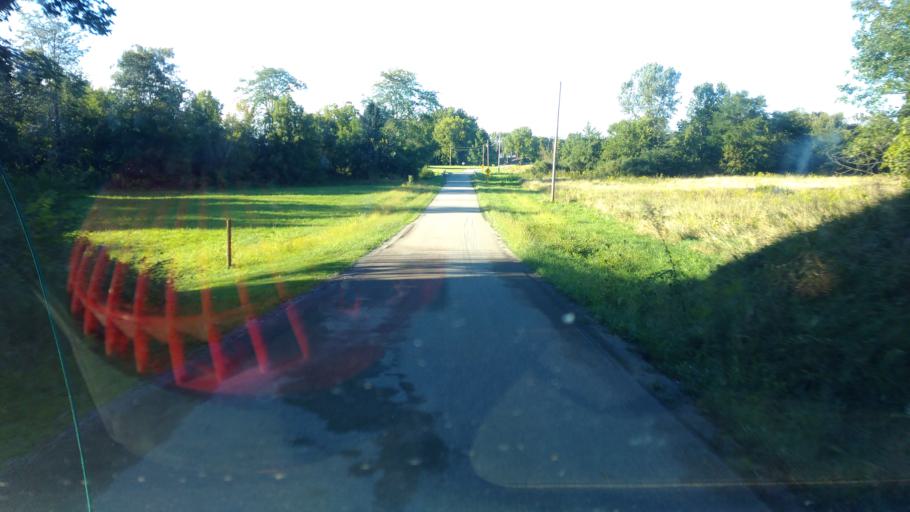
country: US
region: Ohio
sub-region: Wyandot County
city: Upper Sandusky
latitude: 40.8067
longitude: -83.3808
